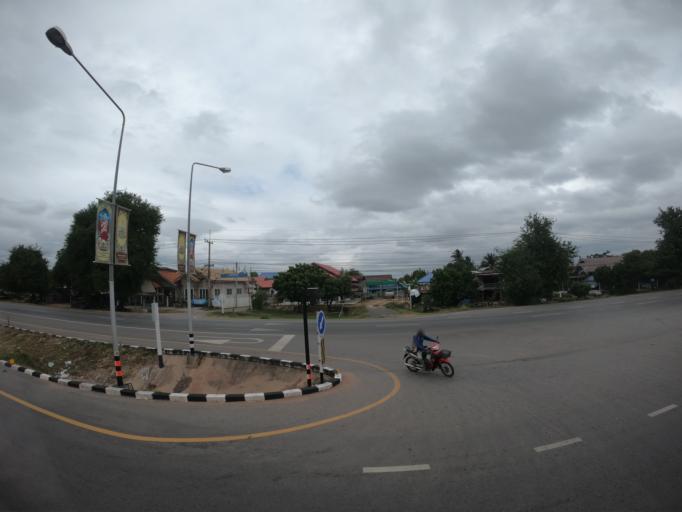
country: TH
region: Khon Kaen
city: Ban Phai
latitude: 16.0443
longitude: 102.8412
